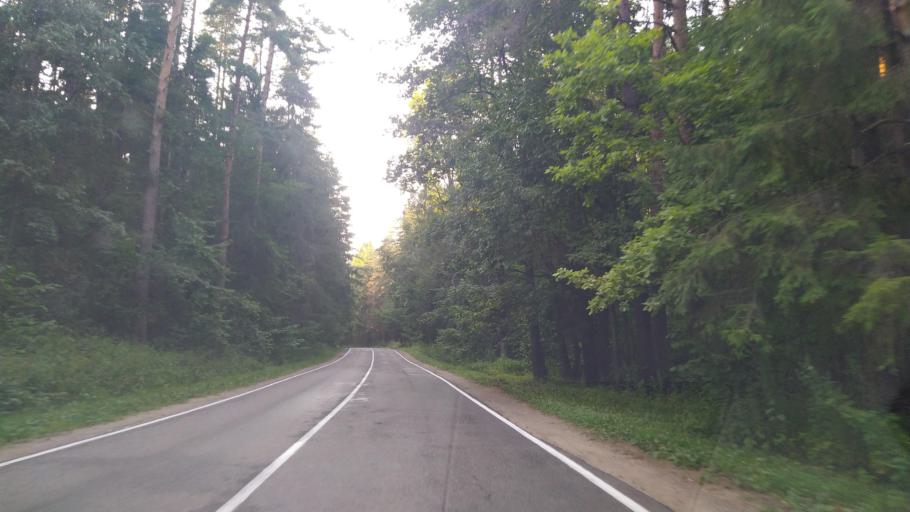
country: RU
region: Pskov
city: Pushkinskiye Gory
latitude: 57.0328
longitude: 28.9203
